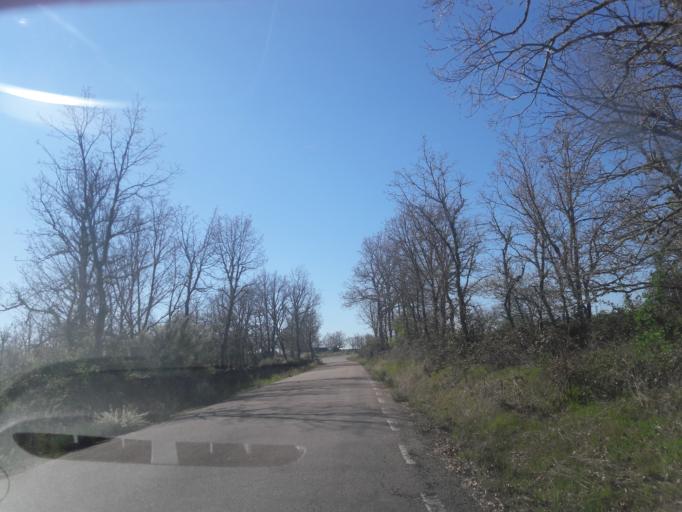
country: ES
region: Castille and Leon
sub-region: Provincia de Salamanca
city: Valsalabroso
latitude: 41.1277
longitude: -6.4819
